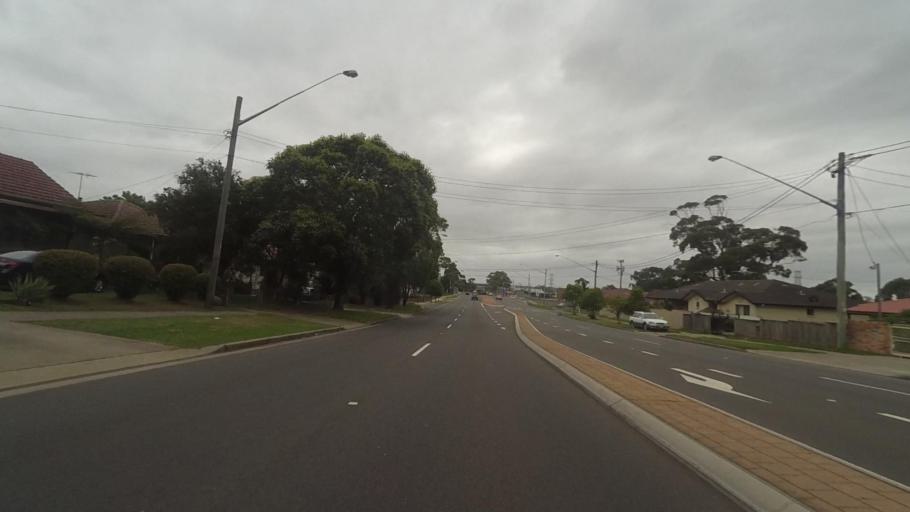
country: AU
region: New South Wales
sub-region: Bankstown
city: Padstow
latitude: -33.9533
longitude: 151.0382
